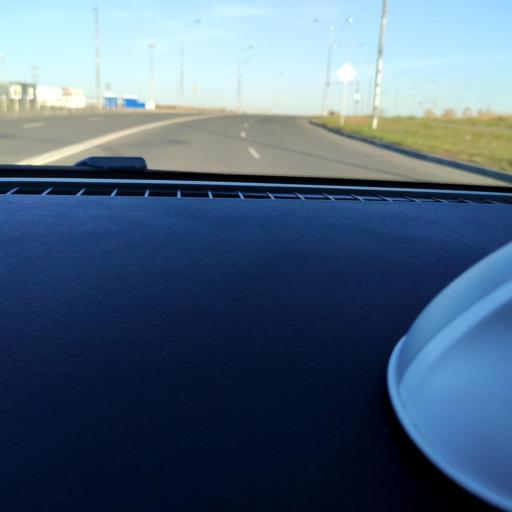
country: RU
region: Samara
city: Samara
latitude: 53.2909
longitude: 50.2304
